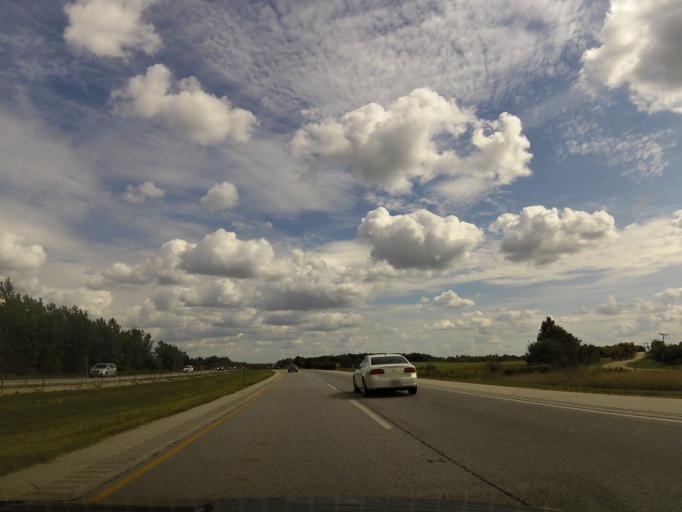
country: US
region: Illinois
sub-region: Kane County
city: Elburn
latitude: 41.8363
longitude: -88.4893
